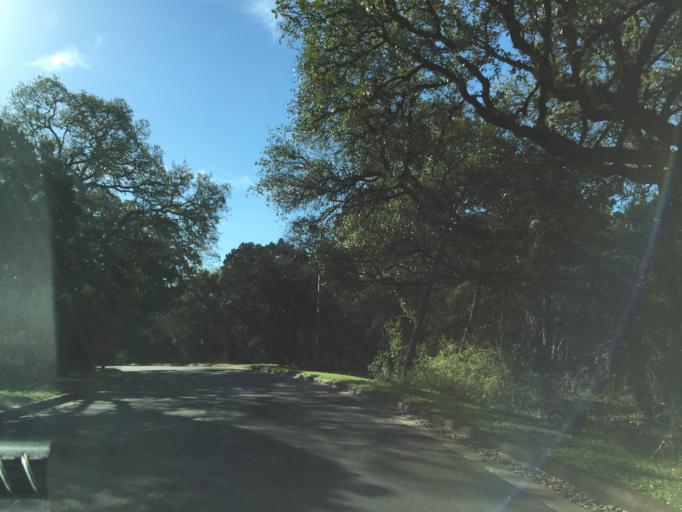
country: US
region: Texas
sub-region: Williamson County
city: Jollyville
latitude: 30.3948
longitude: -97.7371
